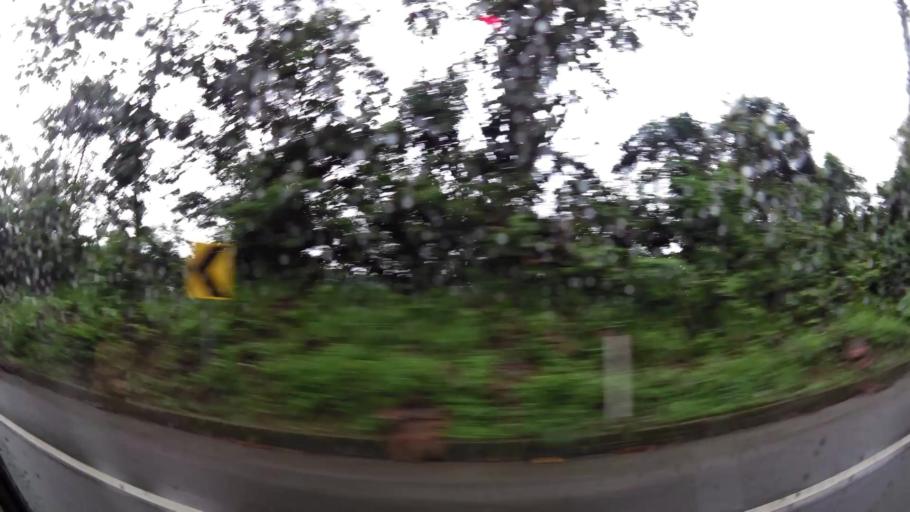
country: EC
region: Santo Domingo de los Tsachilas
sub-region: Canton Santo Domingo de los Colorados
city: Santo Domingo de los Colorados
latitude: -0.2390
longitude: -79.1368
